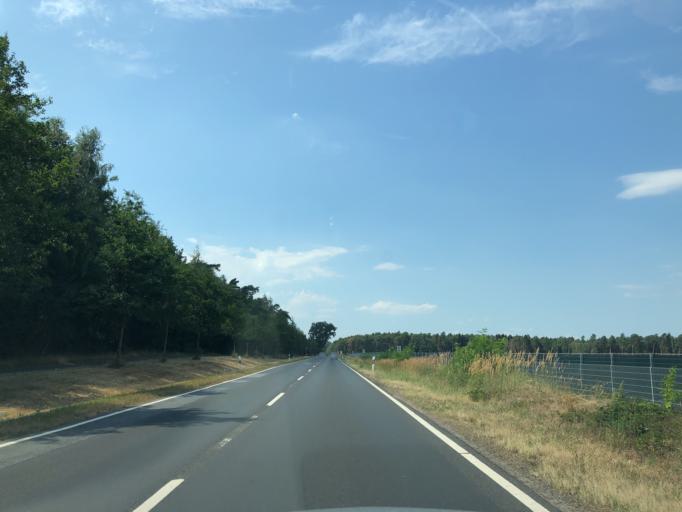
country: DE
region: Hesse
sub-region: Regierungsbezirk Darmstadt
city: Rodgau
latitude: 49.9913
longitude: 8.9106
